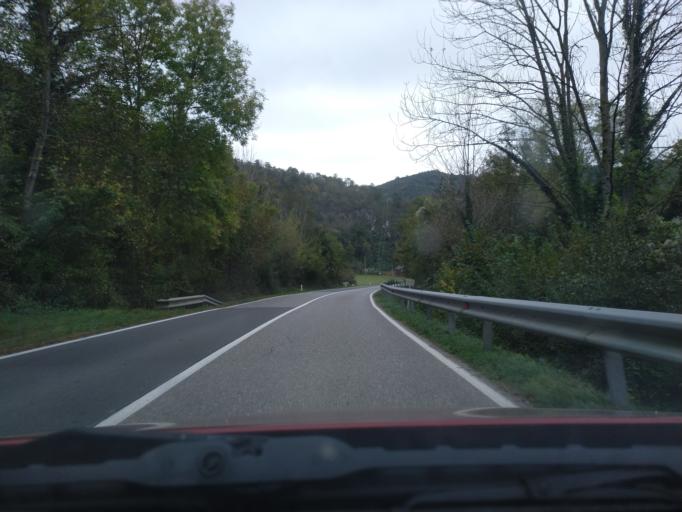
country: SI
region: Kanal
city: Deskle
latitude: 46.0345
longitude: 13.5986
